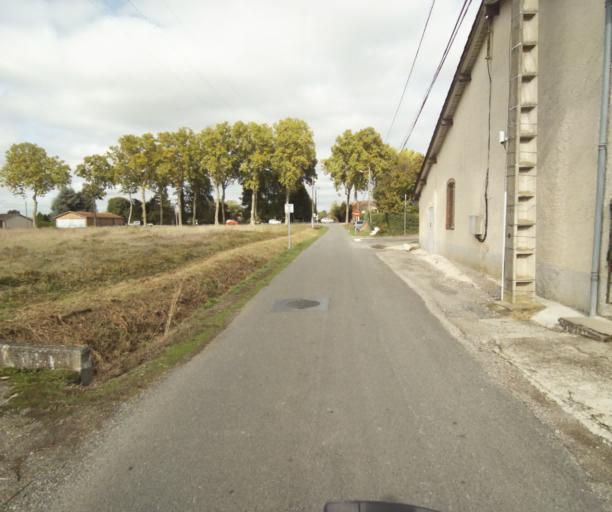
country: FR
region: Midi-Pyrenees
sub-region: Departement du Tarn-et-Garonne
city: Montech
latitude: 43.9549
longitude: 1.2235
